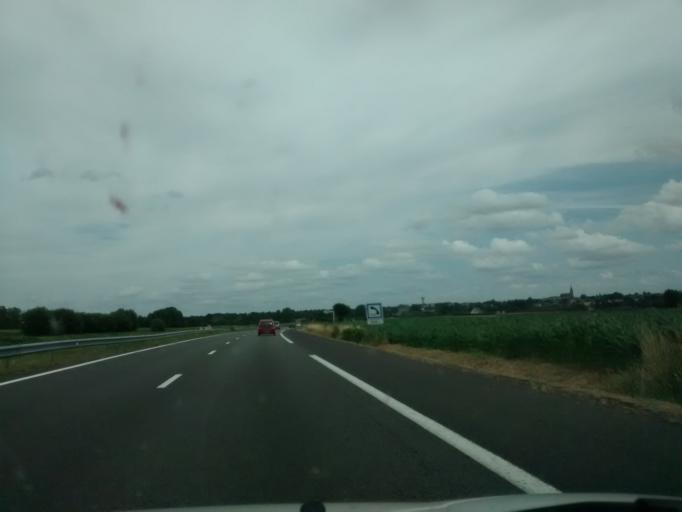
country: FR
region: Brittany
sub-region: Departement d'Ille-et-Vilaine
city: Bedee
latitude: 48.1874
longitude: -1.9711
